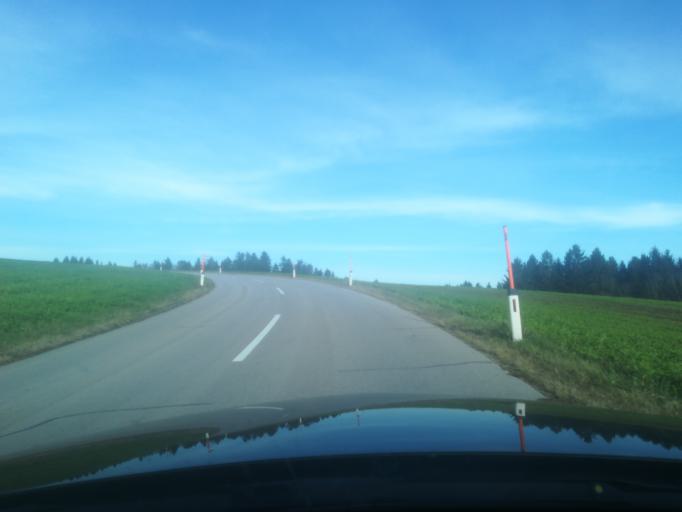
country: AT
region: Upper Austria
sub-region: Politischer Bezirk Perg
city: Perg
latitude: 48.3093
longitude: 14.6625
